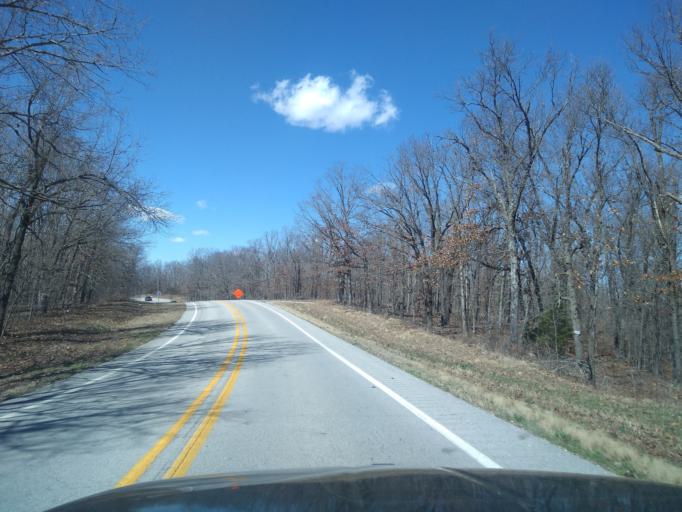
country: US
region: Arkansas
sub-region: Washington County
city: Farmington
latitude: 36.0831
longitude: -94.3209
